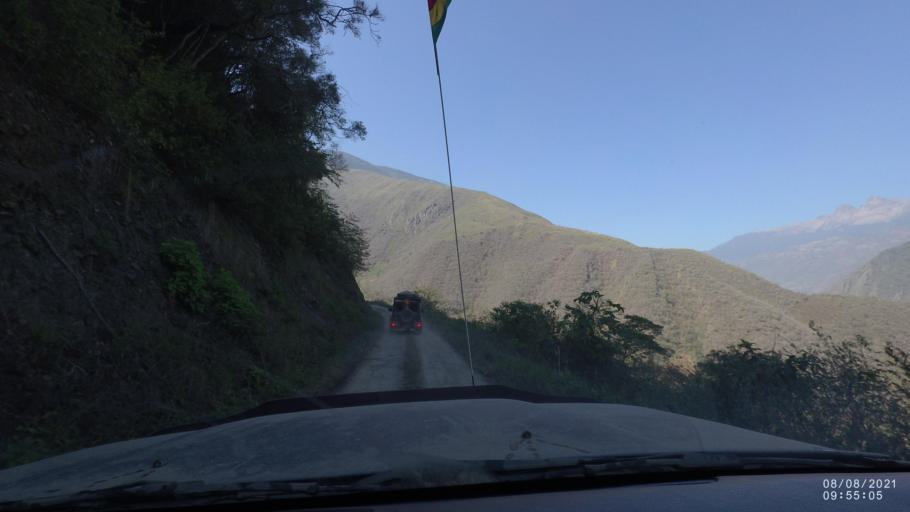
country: BO
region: La Paz
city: Quime
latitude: -16.6337
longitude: -66.7305
